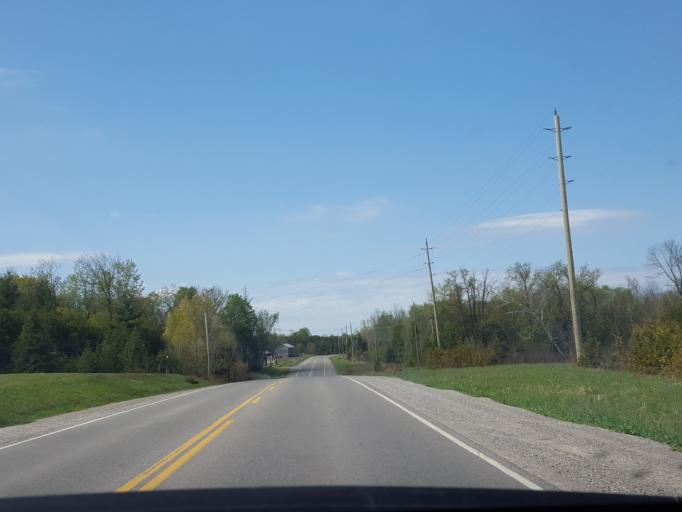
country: CA
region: Ontario
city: Uxbridge
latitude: 44.1504
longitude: -78.9032
